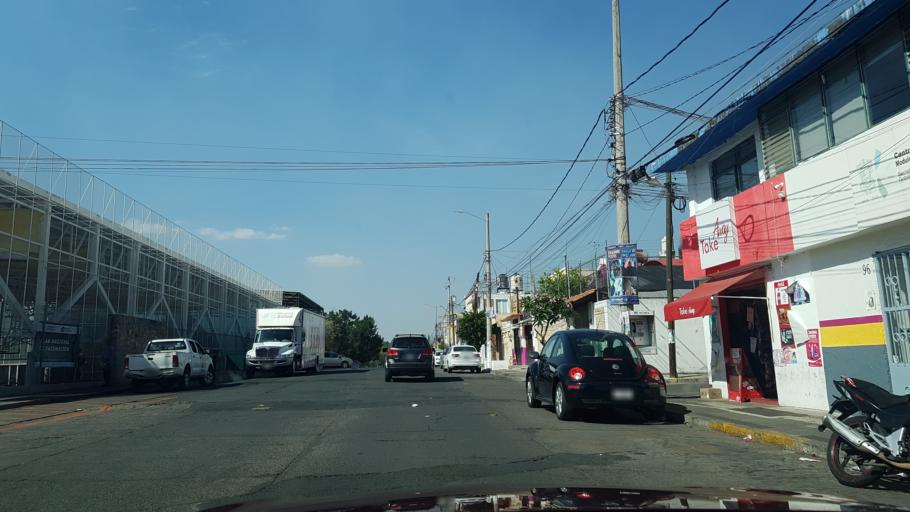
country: MX
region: Michoacan
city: Morelia
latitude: 19.6979
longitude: -101.1674
